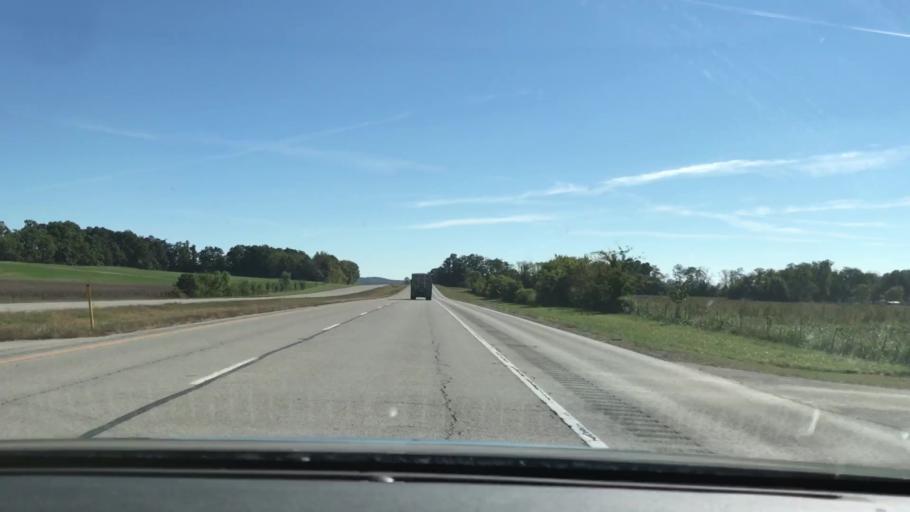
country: US
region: Kentucky
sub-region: Todd County
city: Elkton
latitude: 36.8466
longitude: -87.2972
